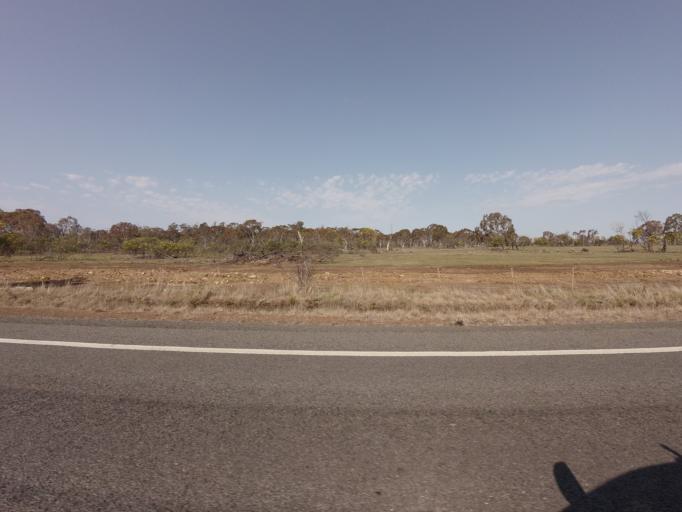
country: AU
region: Tasmania
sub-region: Northern Midlands
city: Evandale
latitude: -41.8343
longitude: 147.4607
